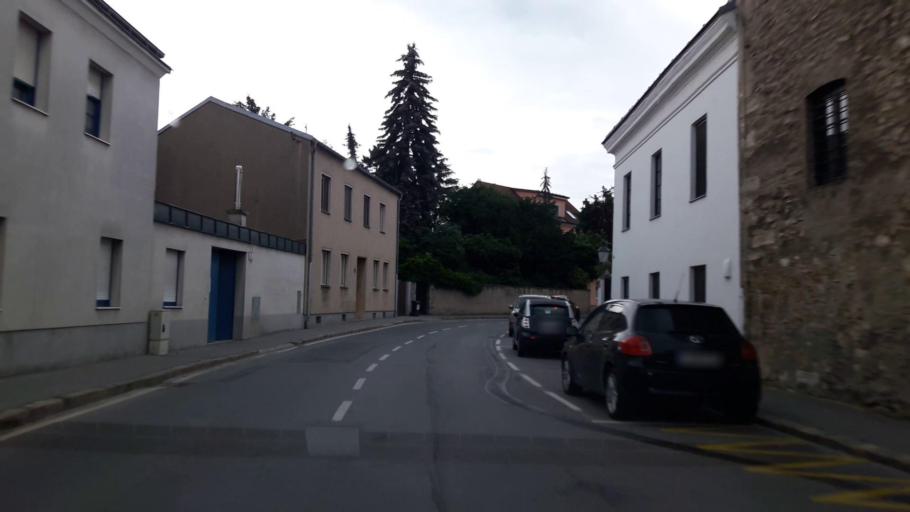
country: AT
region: Burgenland
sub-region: Politischer Bezirk Neusiedl am See
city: Bruckneudorf
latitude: 48.0240
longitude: 16.7808
